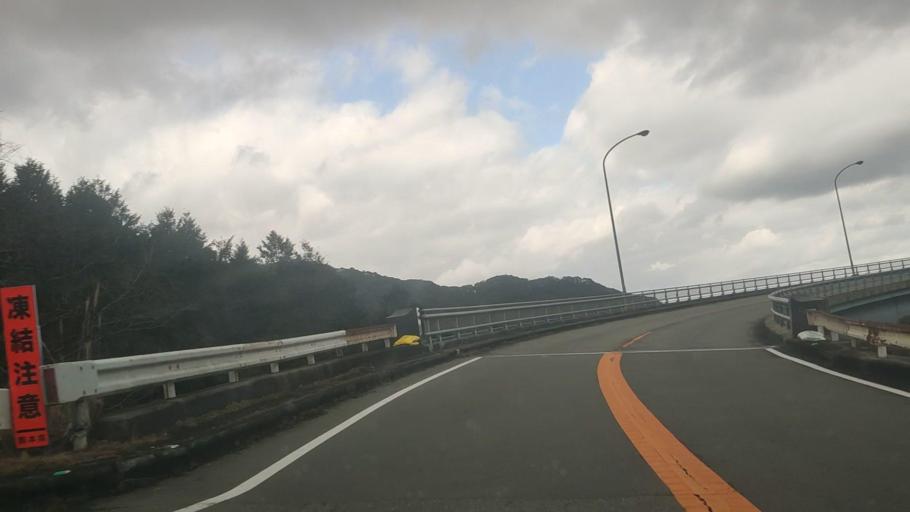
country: JP
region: Kumamoto
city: Hitoyoshi
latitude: 32.1205
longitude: 130.8116
